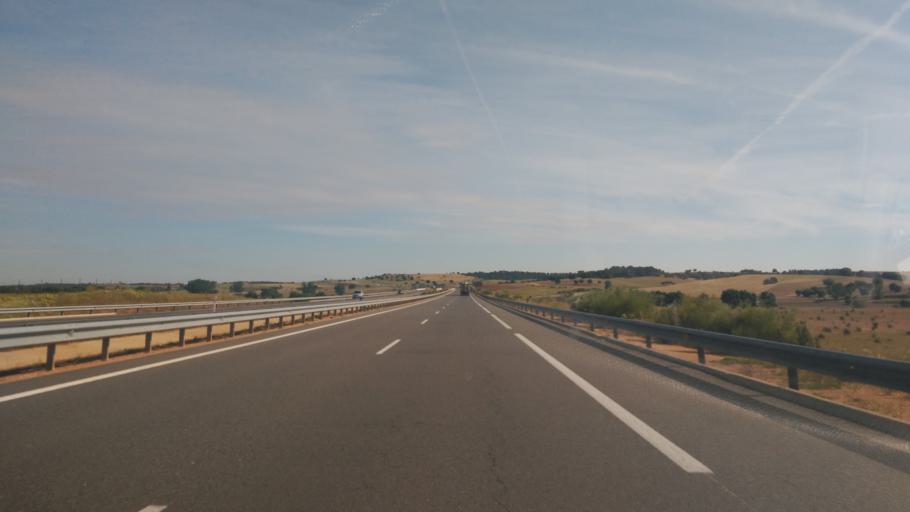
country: ES
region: Castille and Leon
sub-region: Provincia de Zamora
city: Cuelgamures
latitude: 41.2459
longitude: -5.7027
